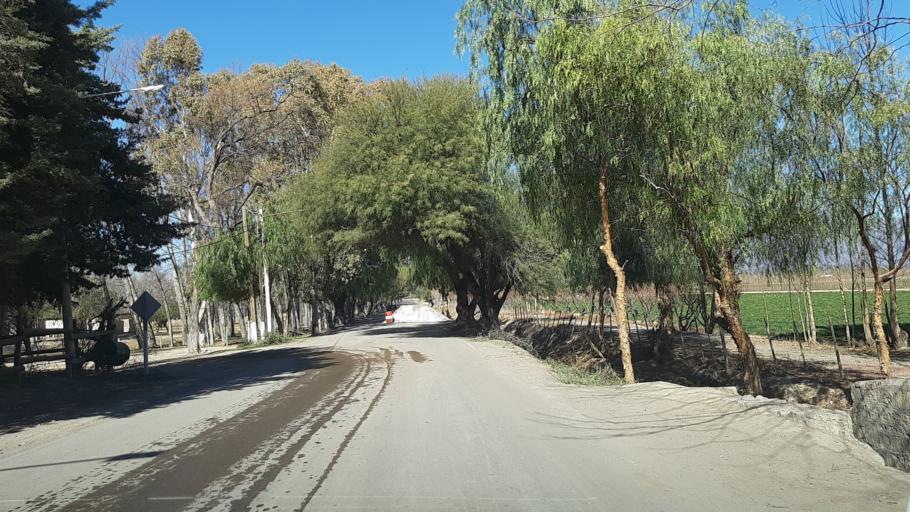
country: AR
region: San Juan
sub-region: Departamento de Zonda
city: Zonda
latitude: -31.4616
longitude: -68.7233
